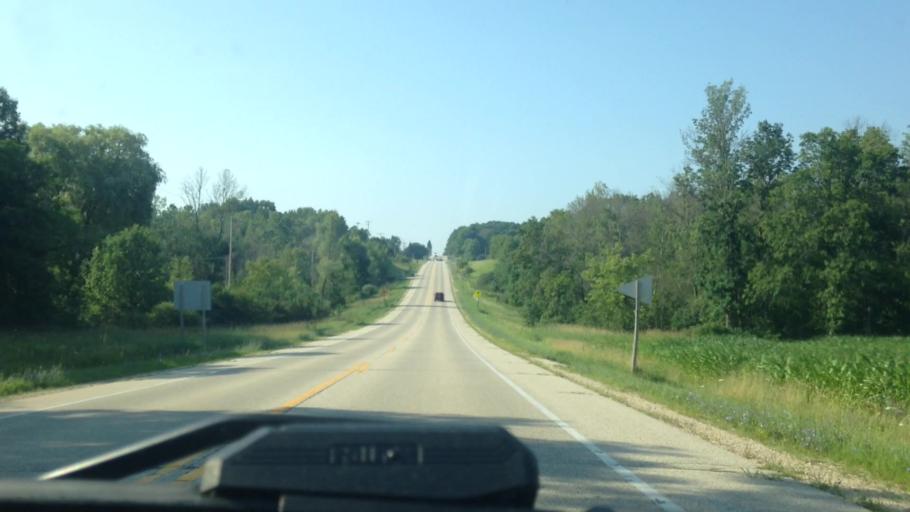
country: US
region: Wisconsin
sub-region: Washington County
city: Richfield
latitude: 43.2570
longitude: -88.2617
